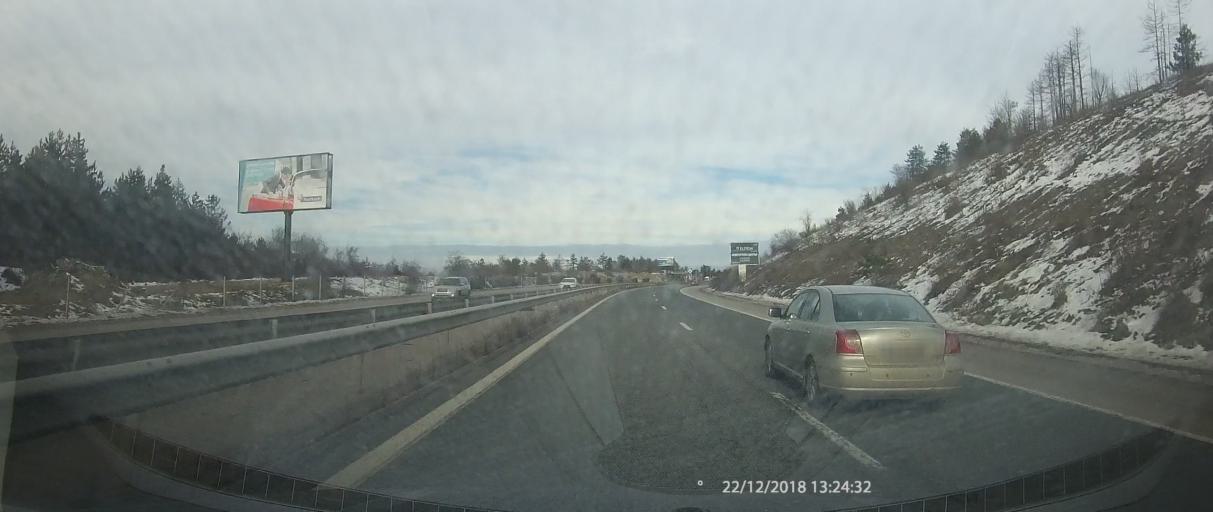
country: BG
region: Lovech
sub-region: Obshtina Yablanitsa
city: Yablanitsa
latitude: 43.0201
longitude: 24.1085
